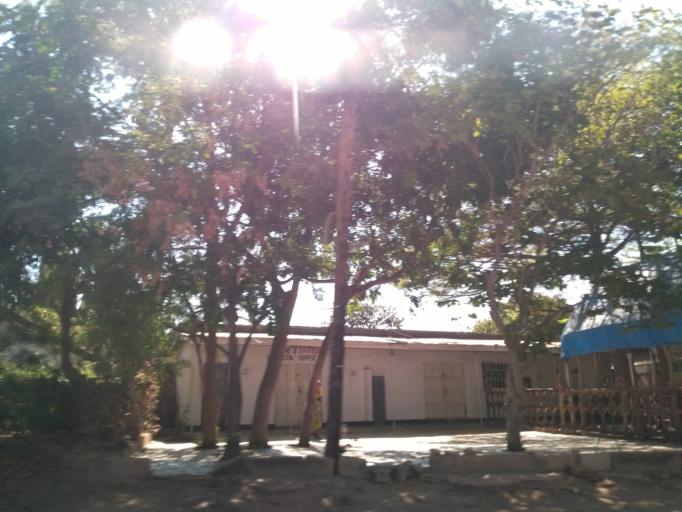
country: TZ
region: Dodoma
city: Dodoma
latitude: -6.1670
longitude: 35.7499
